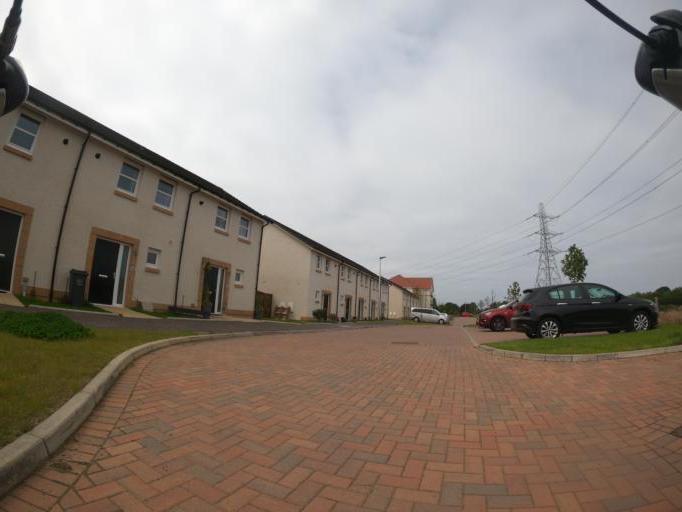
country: GB
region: Scotland
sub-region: East Lothian
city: Musselburgh
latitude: 55.9346
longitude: -3.0831
